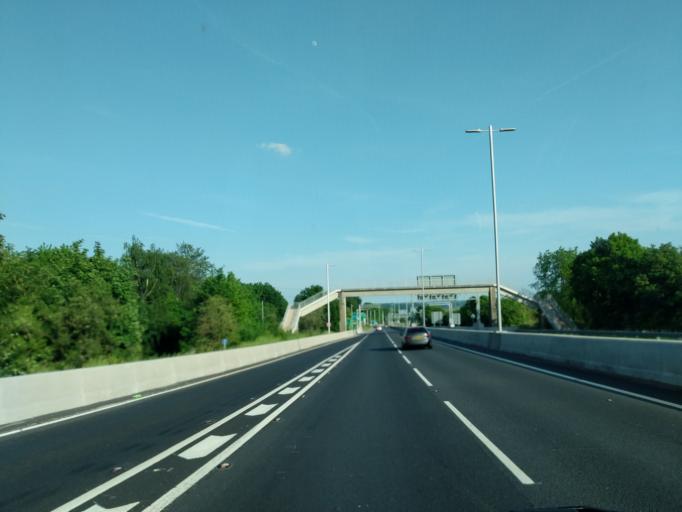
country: GB
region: England
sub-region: Borough of Halton
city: Halton
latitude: 53.3174
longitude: -2.7125
